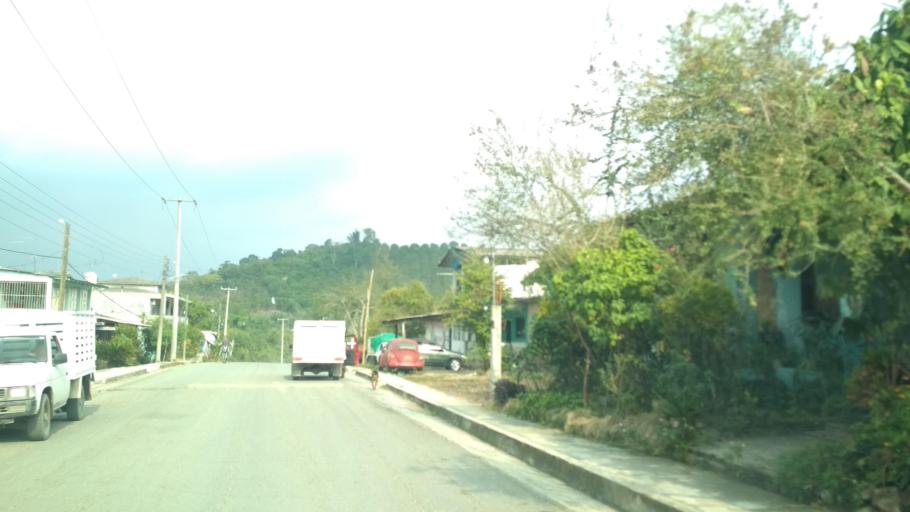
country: MM
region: Kayah
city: Loikaw
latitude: 20.2391
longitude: 97.2765
